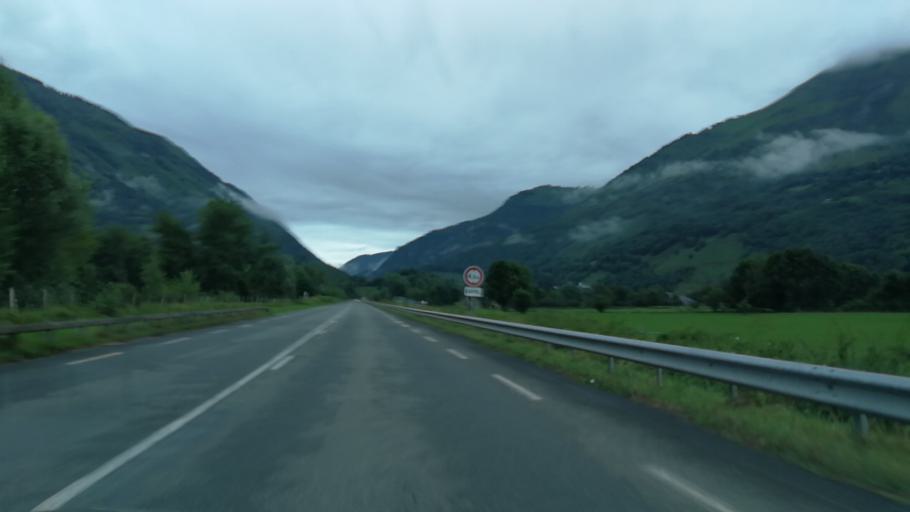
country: FR
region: Aquitaine
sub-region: Departement des Pyrenees-Atlantiques
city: Arette
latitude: 42.9899
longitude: -0.6080
